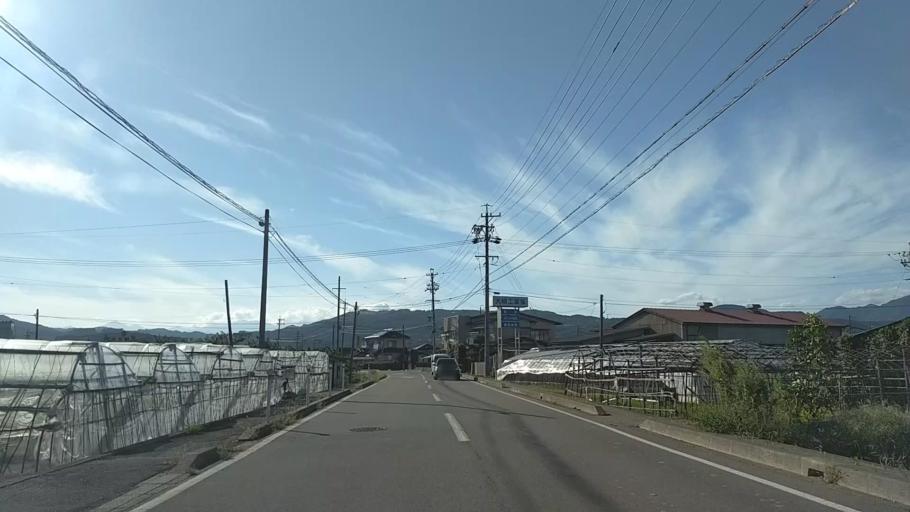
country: JP
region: Nagano
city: Nagano-shi
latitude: 36.5645
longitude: 138.1519
